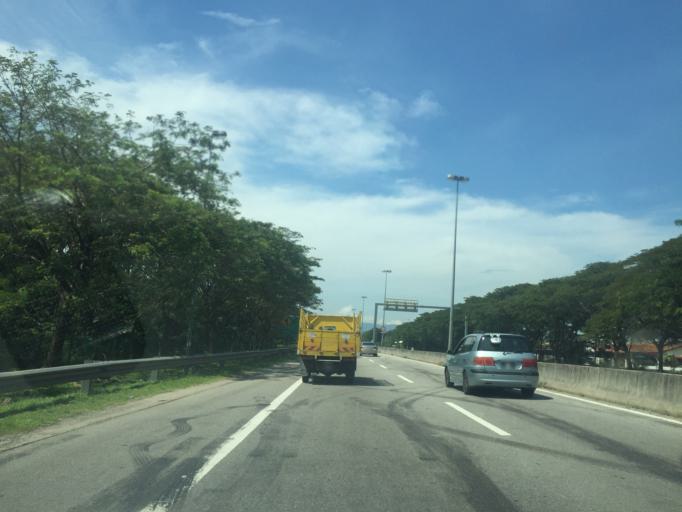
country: MY
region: Penang
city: Permatang Kuching
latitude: 5.4470
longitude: 100.4014
